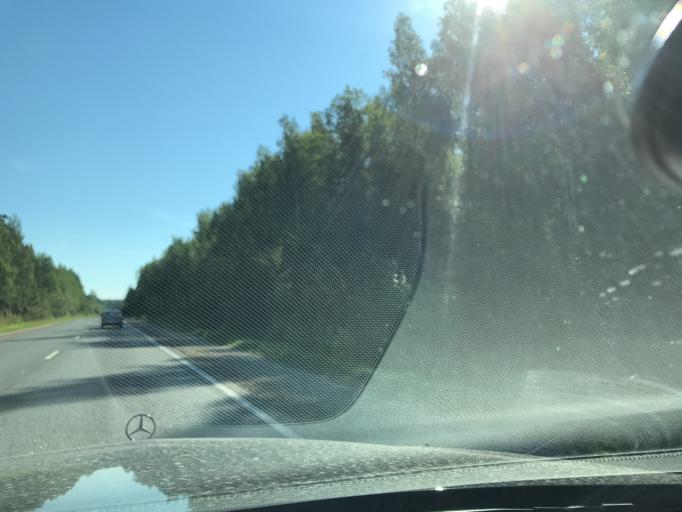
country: RU
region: Vladimir
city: Kirzhach
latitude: 56.1116
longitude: 38.7304
